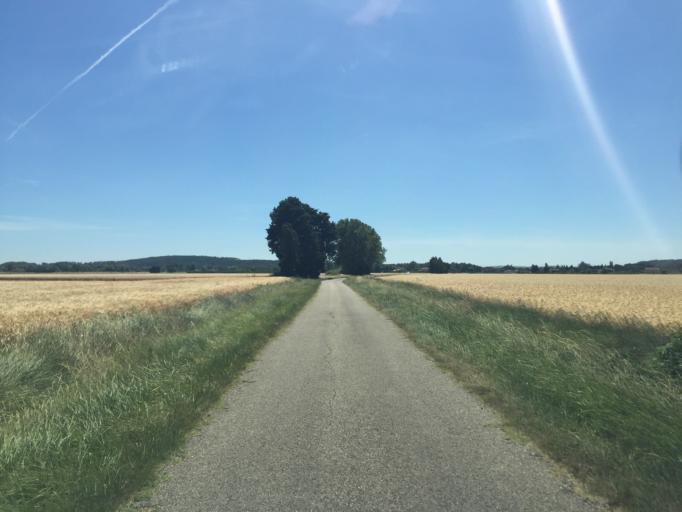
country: FR
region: Provence-Alpes-Cote d'Azur
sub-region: Departement du Vaucluse
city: Bedarrides
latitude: 44.0505
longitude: 4.9178
